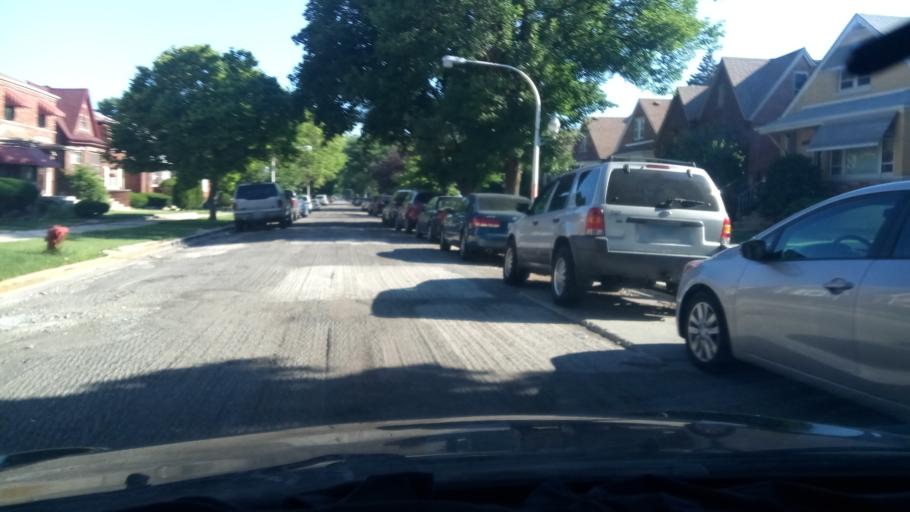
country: US
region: Illinois
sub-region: Cook County
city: Hometown
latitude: 41.7736
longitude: -87.7238
